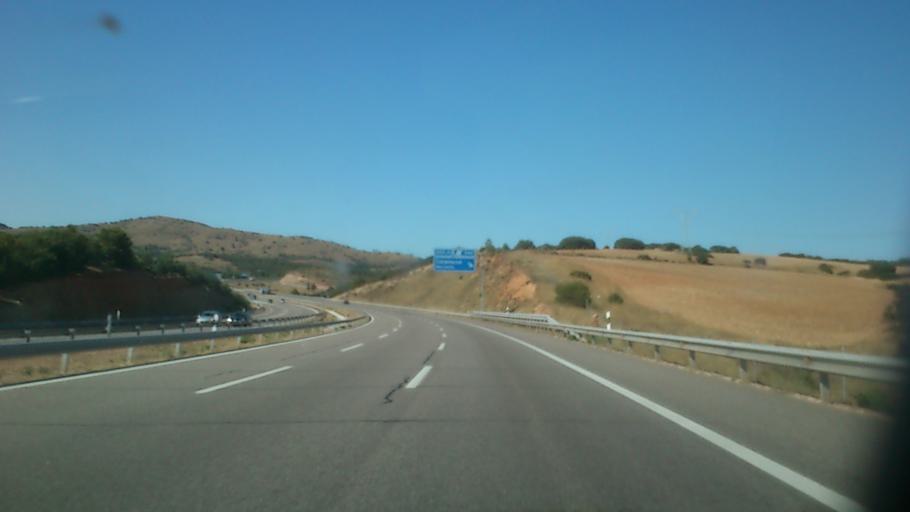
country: ES
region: Aragon
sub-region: Provincia de Zaragoza
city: Sediles
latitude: 41.3737
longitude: -1.5735
